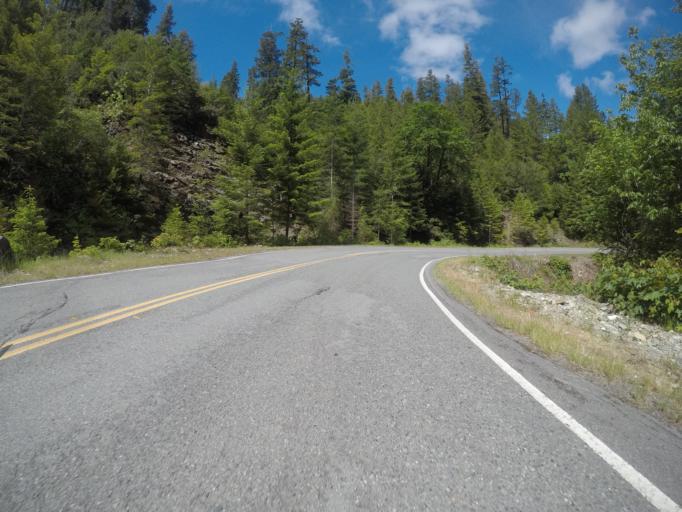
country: US
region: California
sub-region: Del Norte County
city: Bertsch-Oceanview
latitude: 41.7226
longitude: -123.9528
